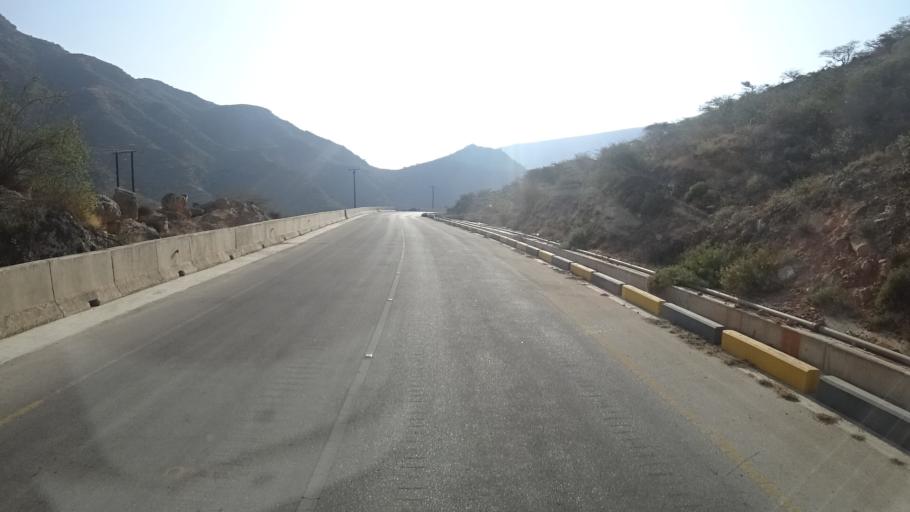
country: YE
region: Al Mahrah
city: Hawf
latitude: 16.7471
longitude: 53.2277
